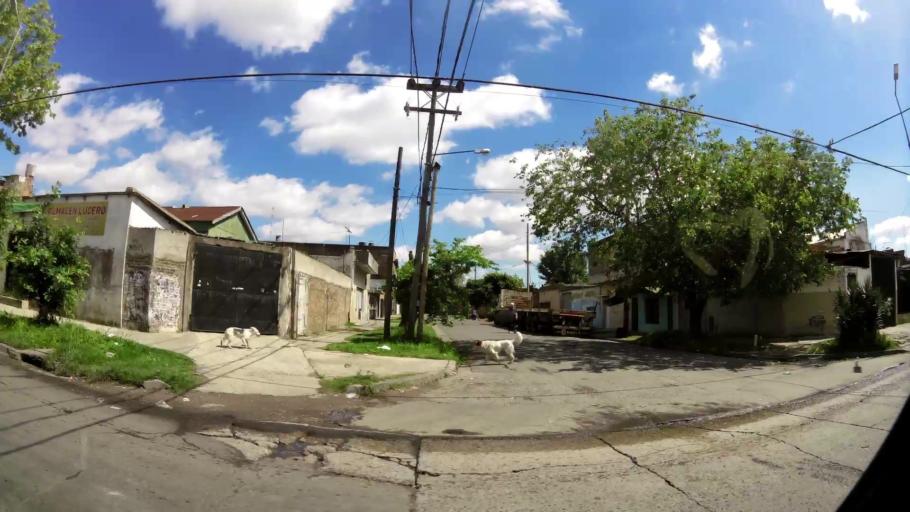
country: AR
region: Buenos Aires
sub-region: Partido de Lanus
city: Lanus
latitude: -34.6745
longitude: -58.4289
